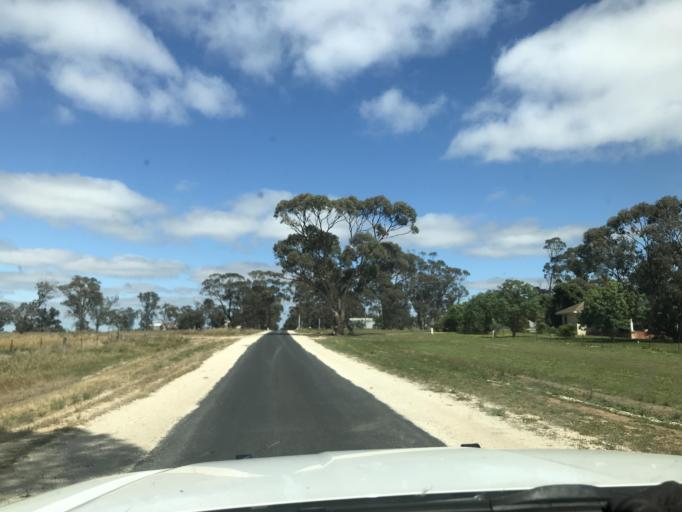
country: AU
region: South Australia
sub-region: Tatiara
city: Bordertown
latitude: -36.3062
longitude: 141.0773
